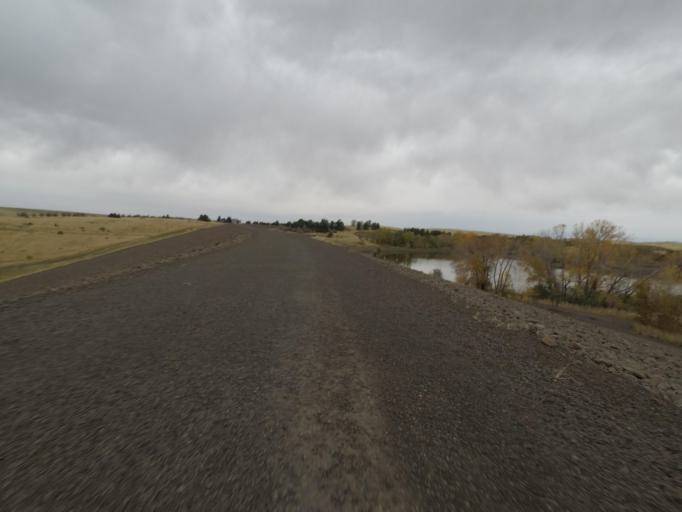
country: US
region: Washington
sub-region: Walla Walla County
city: Walla Walla East
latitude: 46.0628
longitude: -118.2613
